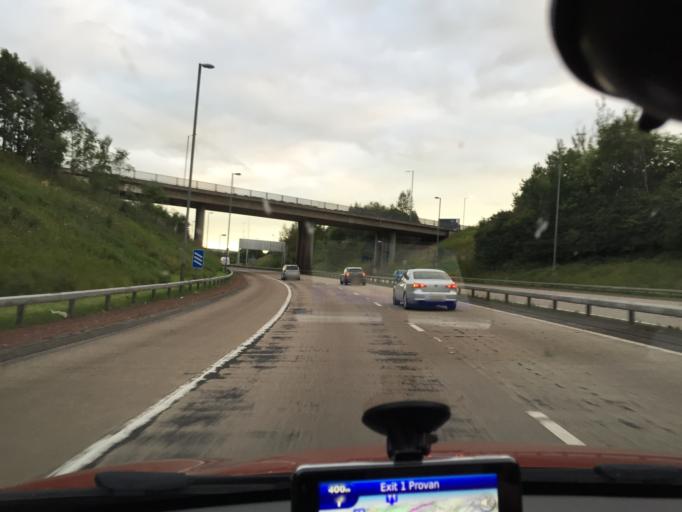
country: GB
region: Scotland
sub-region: East Dunbartonshire
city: Bishopbriggs
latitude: 55.8791
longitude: -4.1977
